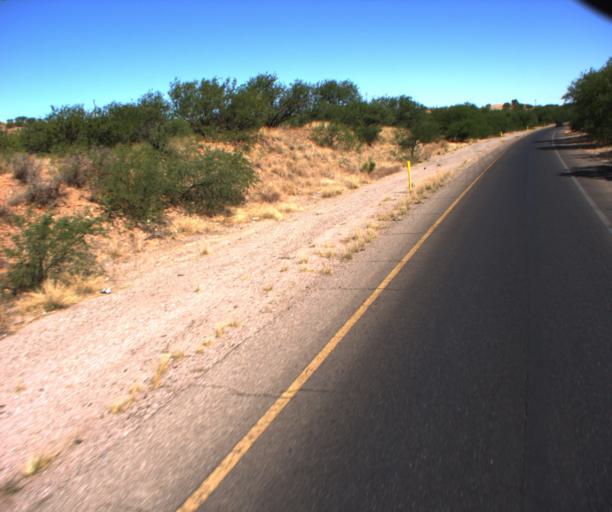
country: US
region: Arizona
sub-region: Santa Cruz County
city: Nogales
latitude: 31.3973
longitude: -110.9589
